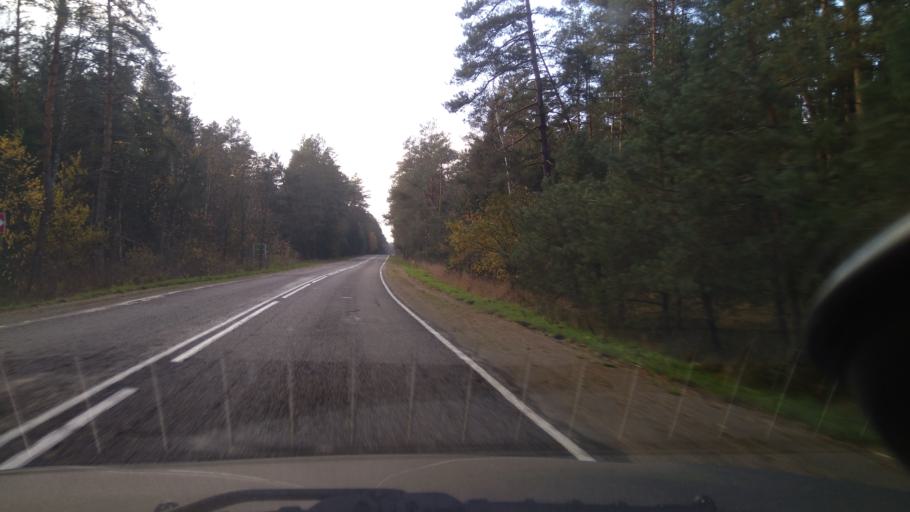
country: BY
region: Minsk
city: Slutsk
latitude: 53.2228
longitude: 27.6025
